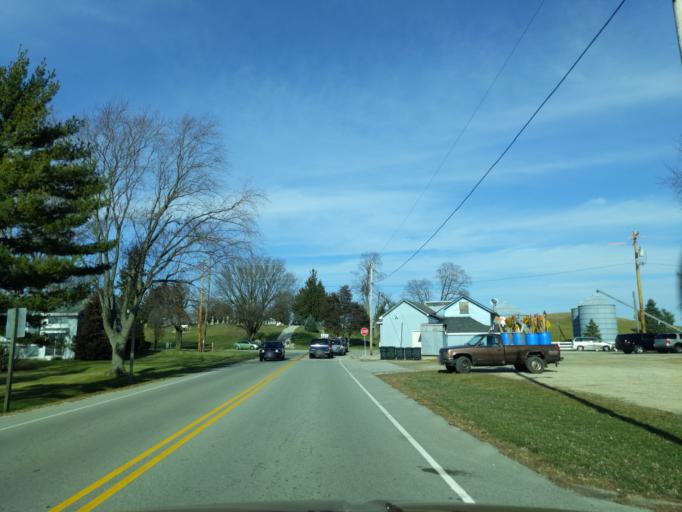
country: US
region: Wisconsin
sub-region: Walworth County
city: Elkhorn
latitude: 42.7338
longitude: -88.5822
